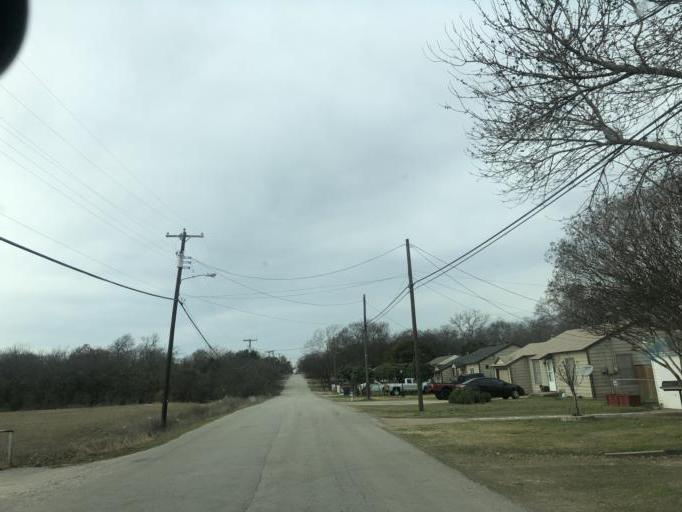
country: US
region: Texas
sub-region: Dallas County
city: Duncanville
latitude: 32.6693
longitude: -96.8244
